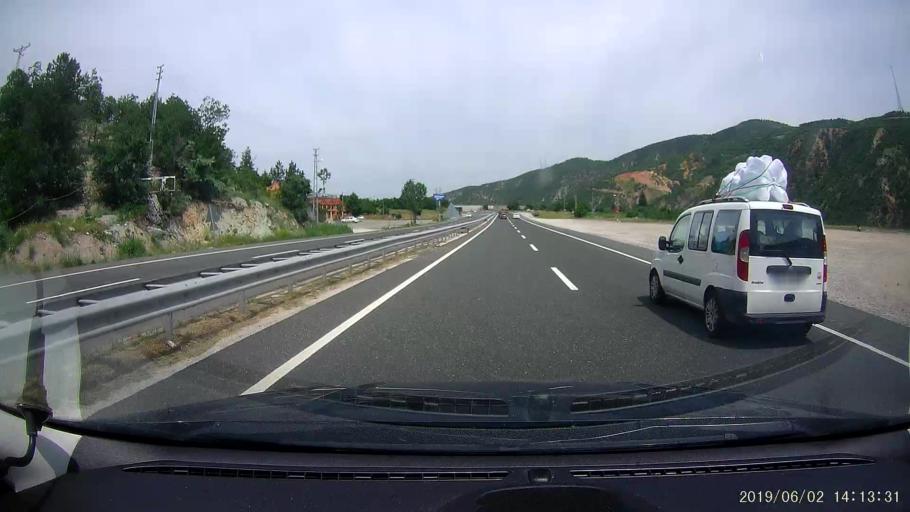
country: TR
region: Cankiri
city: Yaprakli
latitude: 40.9266
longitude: 33.8318
